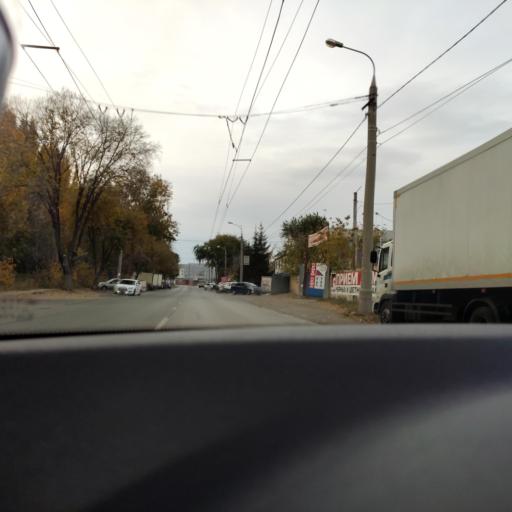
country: RU
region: Samara
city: Samara
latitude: 53.2002
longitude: 50.2666
